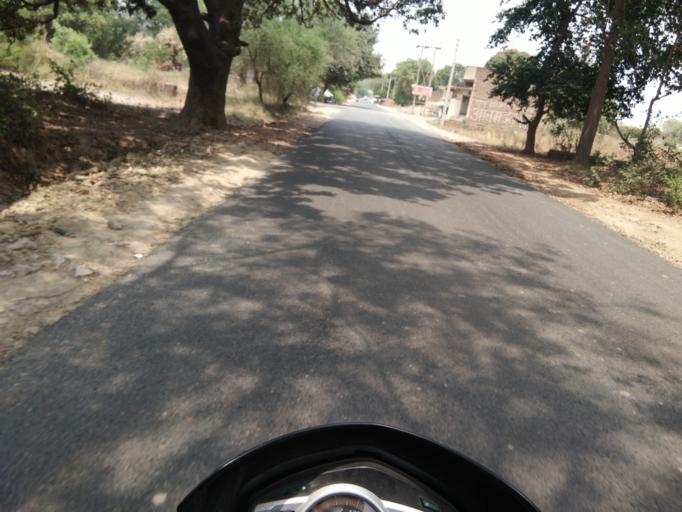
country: IN
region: Uttar Pradesh
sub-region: Ghazipur
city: Zamania
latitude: 25.4376
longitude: 83.6834
